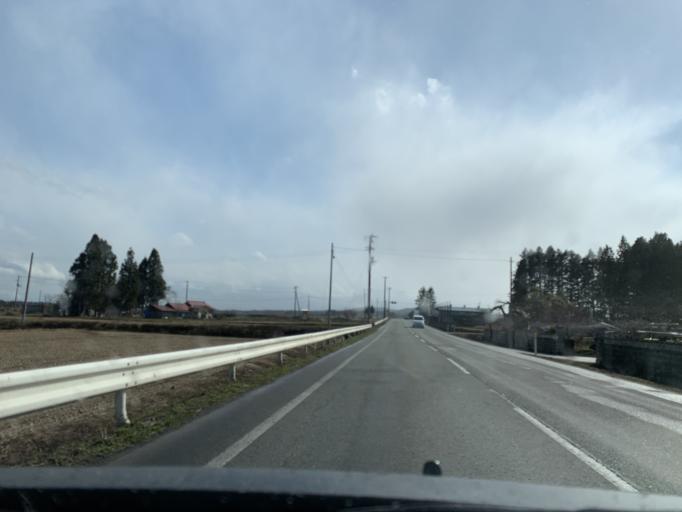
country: JP
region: Iwate
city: Kitakami
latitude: 39.2085
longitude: 141.0563
